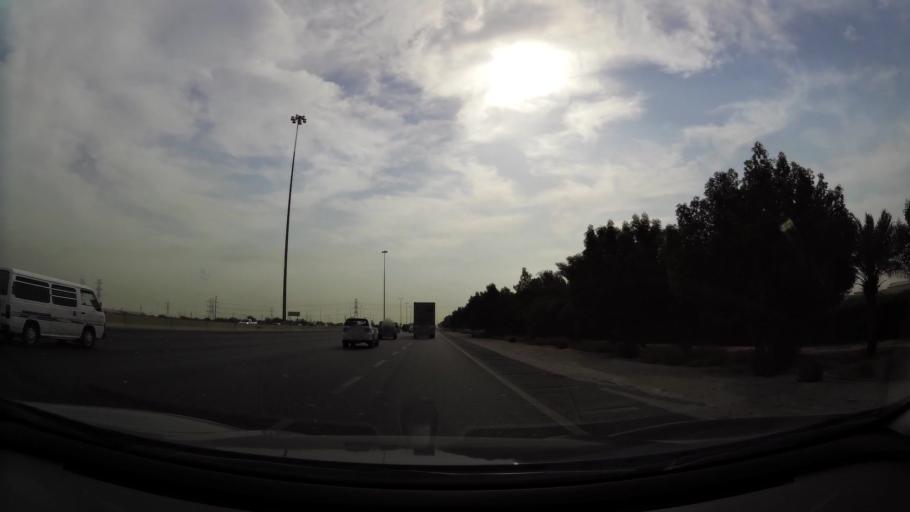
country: KW
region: Muhafazat al Jahra'
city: Al Jahra'
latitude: 29.3206
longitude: 47.7572
